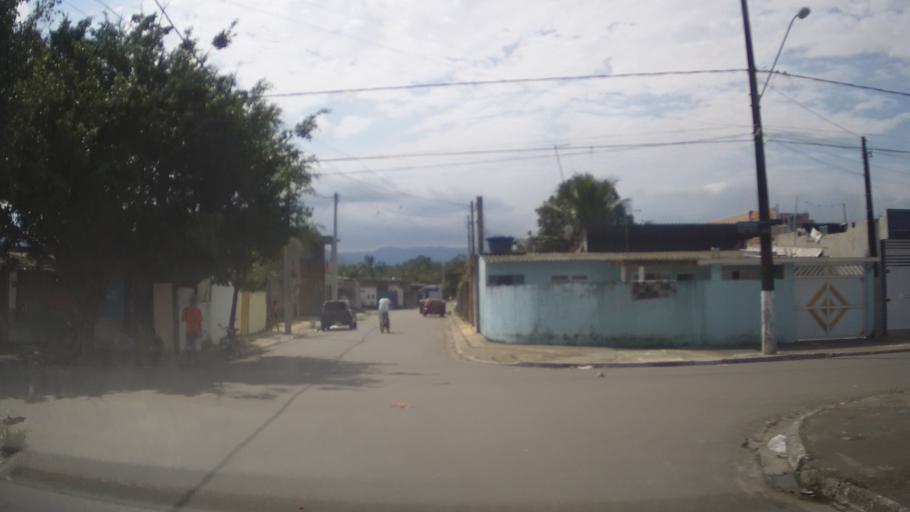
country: BR
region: Sao Paulo
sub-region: Praia Grande
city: Praia Grande
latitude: -24.0036
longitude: -46.4394
